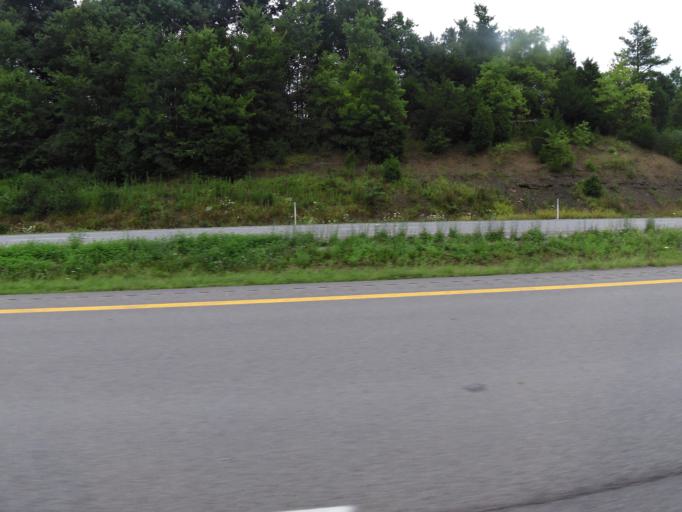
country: US
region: Kentucky
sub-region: Grayson County
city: Leitchfield
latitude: 37.4086
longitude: -86.4674
